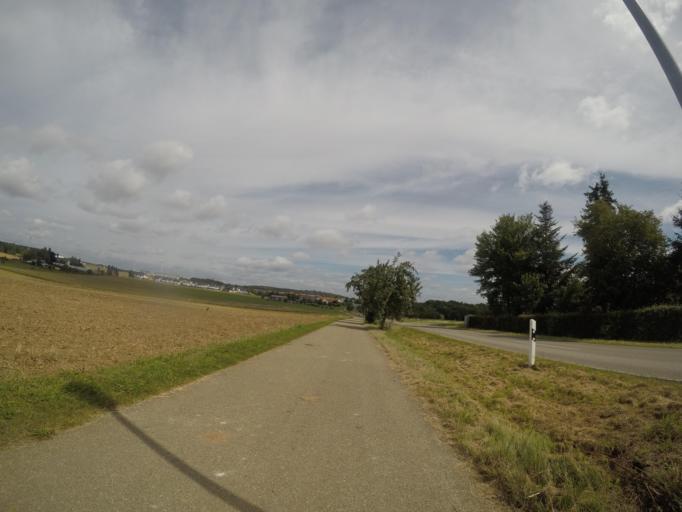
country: DE
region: Baden-Wuerttemberg
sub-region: Tuebingen Region
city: Blaubeuren
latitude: 48.4192
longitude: 9.7511
